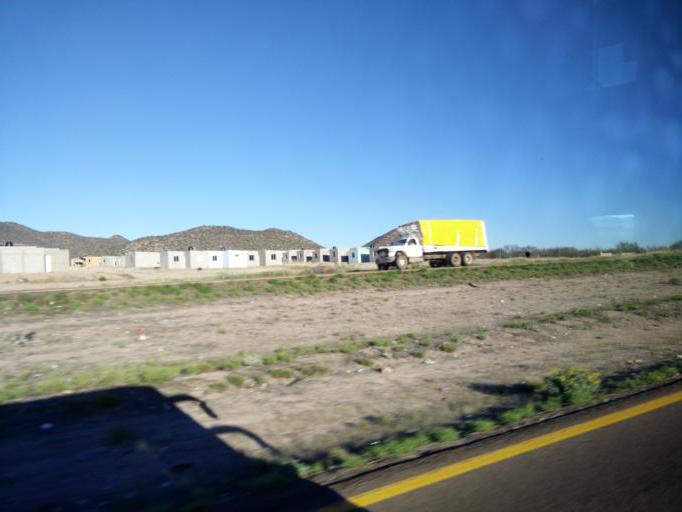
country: MX
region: Sonora
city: Heroica Guaymas
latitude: 28.0028
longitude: -110.9364
